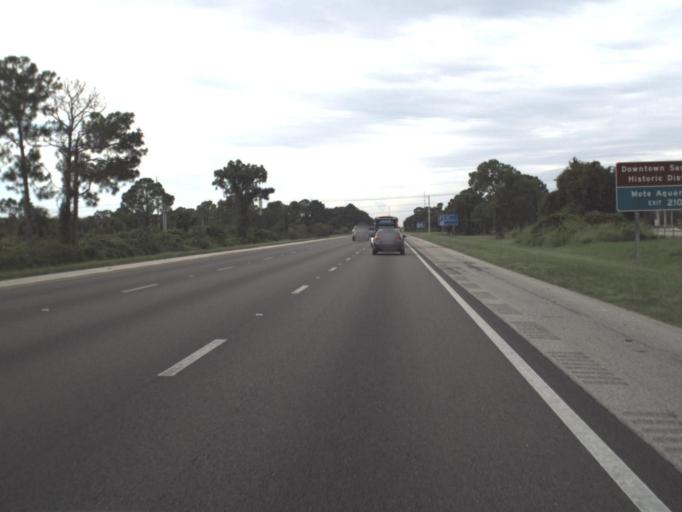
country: US
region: Florida
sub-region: Sarasota County
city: The Meadows
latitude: 27.3611
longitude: -82.4468
